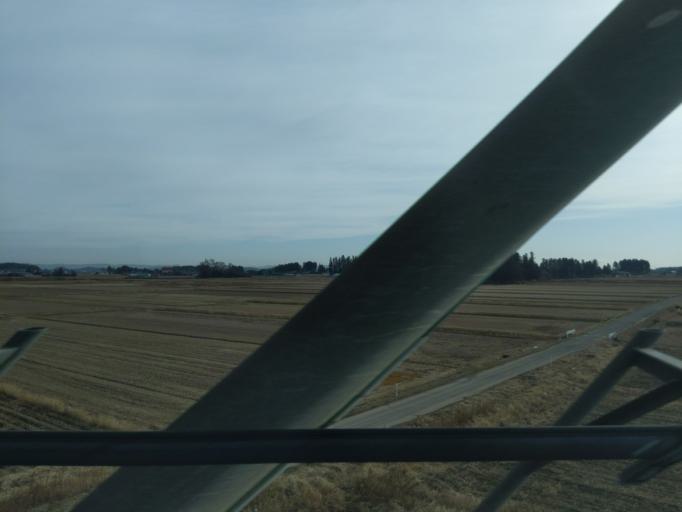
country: JP
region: Iwate
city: Ichinoseki
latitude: 38.7725
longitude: 141.0851
